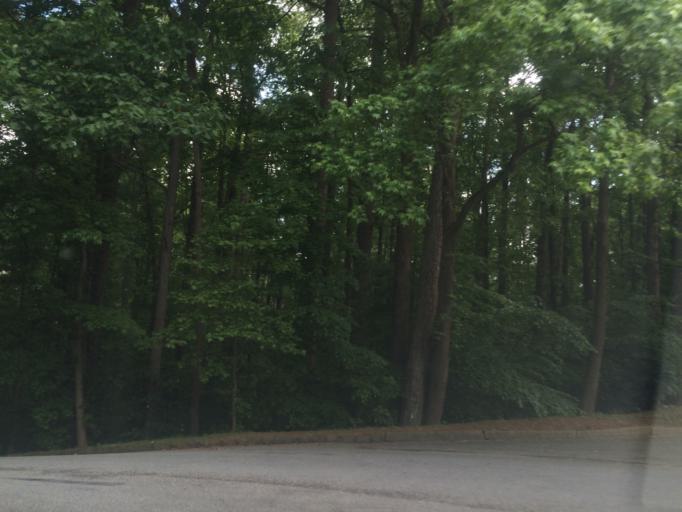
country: US
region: Georgia
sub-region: DeKalb County
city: Druid Hills
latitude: 33.8003
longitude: -84.3534
